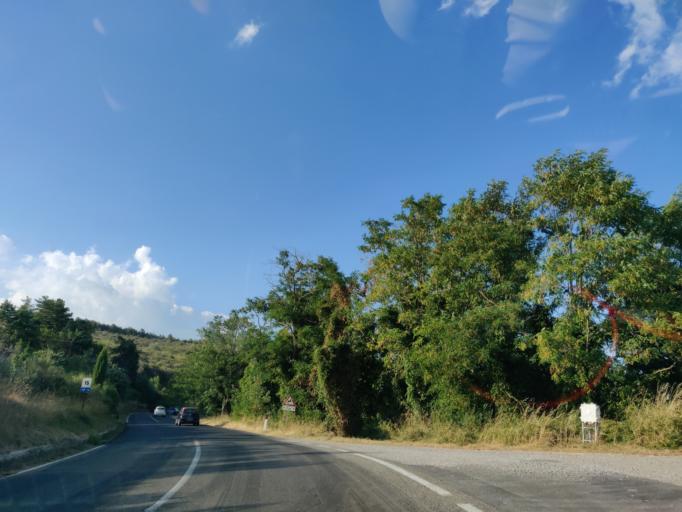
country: IT
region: Tuscany
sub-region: Provincia di Siena
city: Abbadia San Salvatore
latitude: 42.8674
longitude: 11.6814
